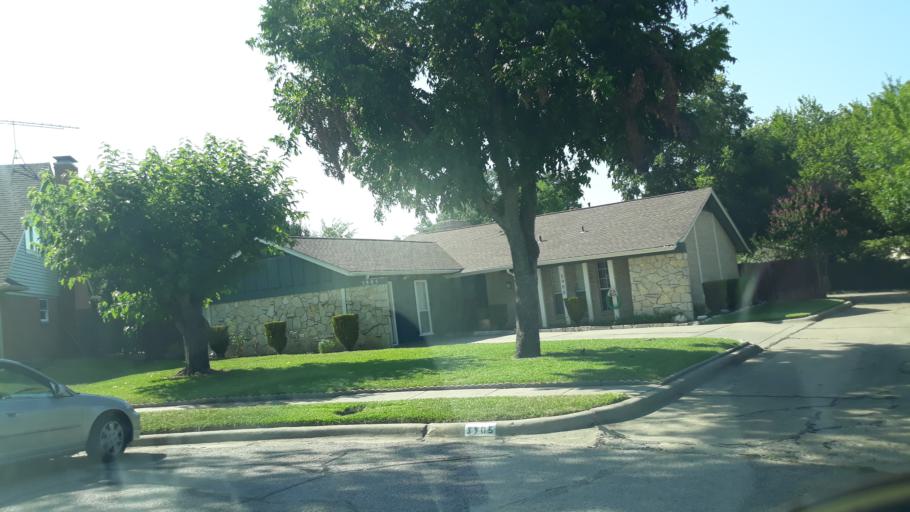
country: US
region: Texas
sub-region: Dallas County
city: Irving
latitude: 32.8478
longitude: -97.0036
